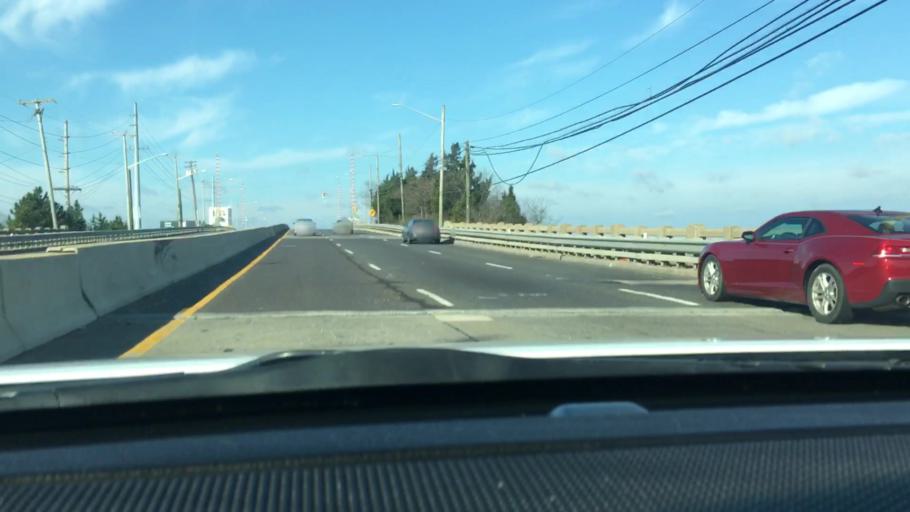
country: US
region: New Jersey
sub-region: Atlantic County
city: Atlantic City
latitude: 39.3767
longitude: -74.4500
